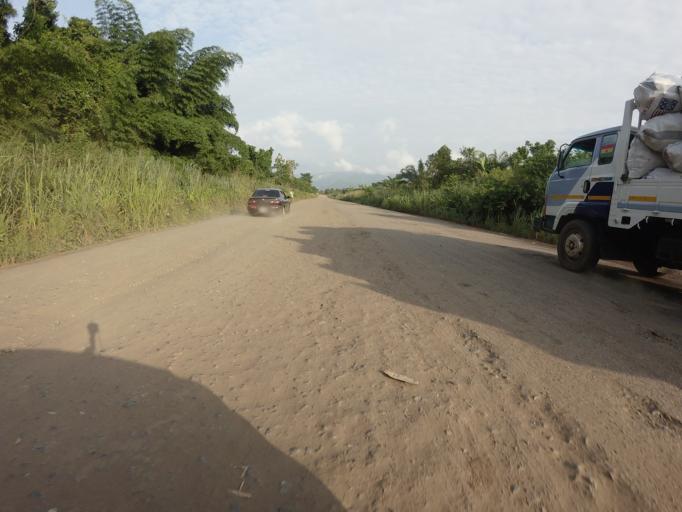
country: GH
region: Volta
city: Kpandu
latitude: 6.9731
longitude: 0.4518
